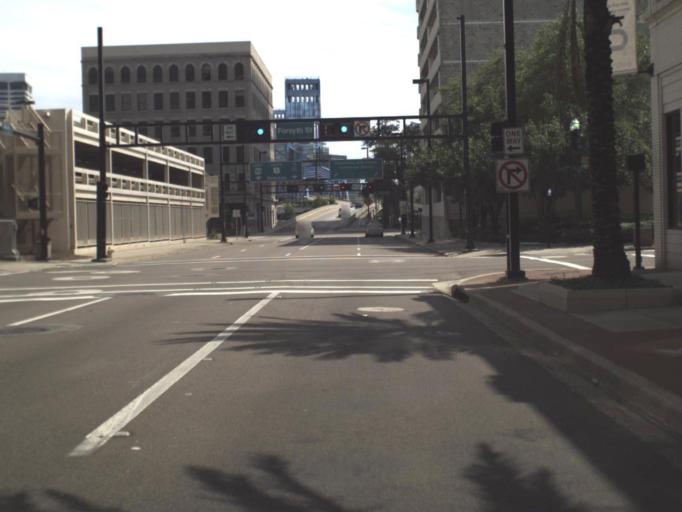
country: US
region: Florida
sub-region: Duval County
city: Jacksonville
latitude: 30.3273
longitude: -81.6577
